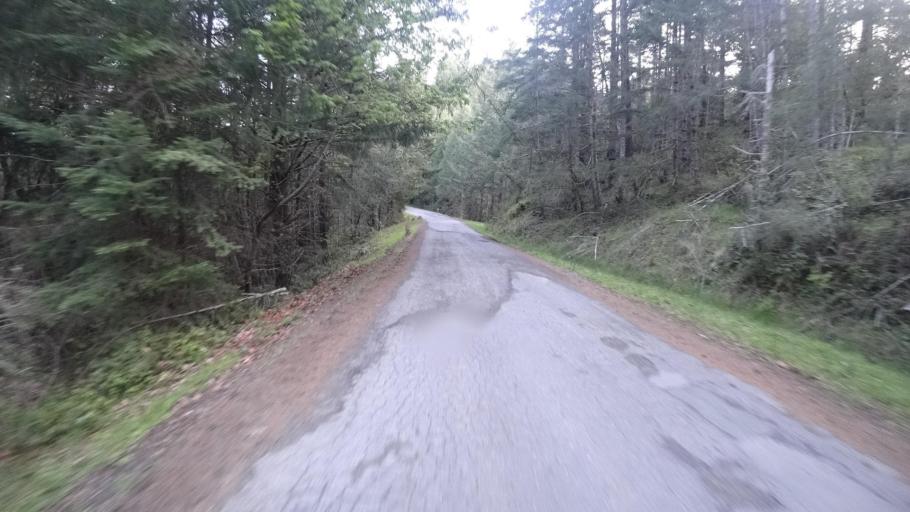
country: US
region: California
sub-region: Humboldt County
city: Bayside
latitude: 40.6830
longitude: -123.9370
